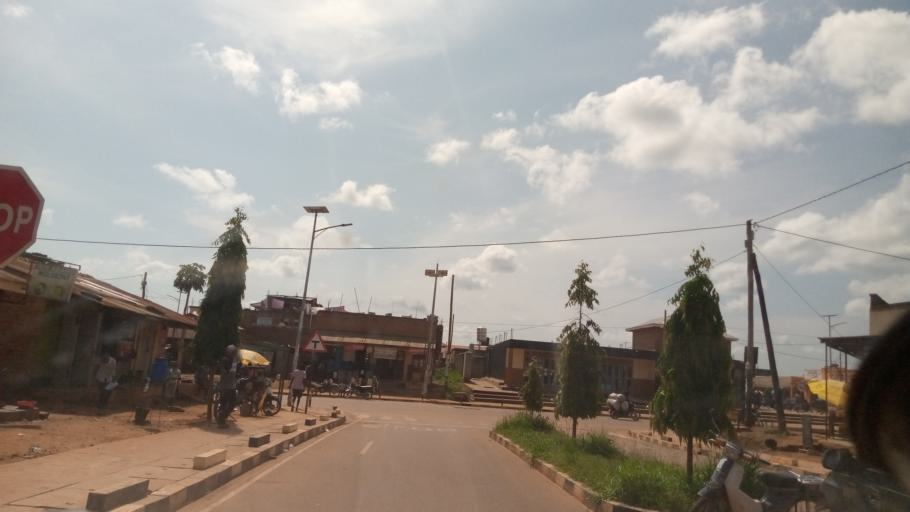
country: UG
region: Northern Region
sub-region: Gulu District
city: Gulu
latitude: 2.7695
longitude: 32.3047
